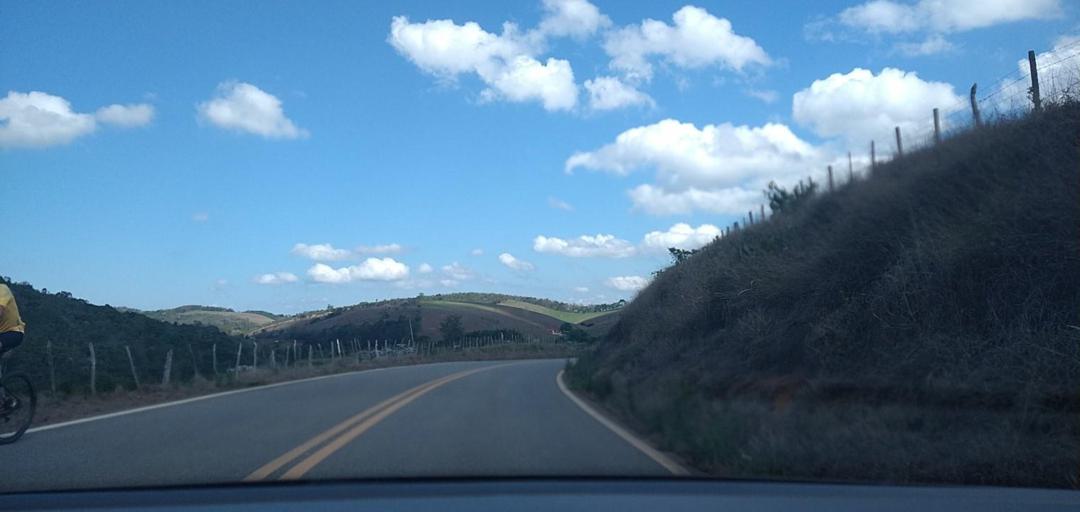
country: BR
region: Minas Gerais
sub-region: Alvinopolis
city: Alvinopolis
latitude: -20.0225
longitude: -43.0637
